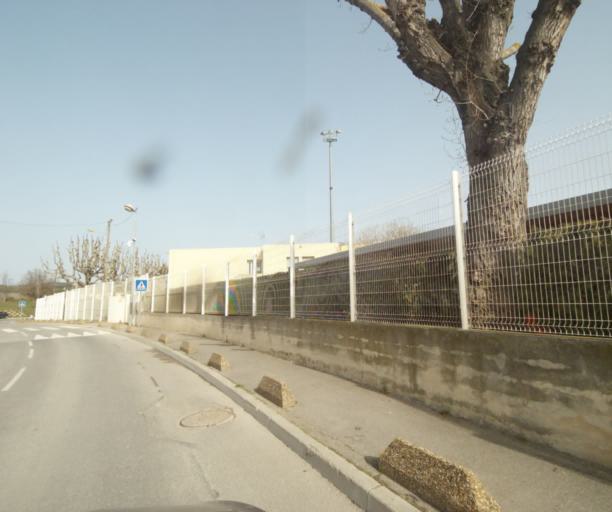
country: FR
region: Provence-Alpes-Cote d'Azur
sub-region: Departement des Bouches-du-Rhone
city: Meyreuil
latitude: 43.4710
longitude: 5.4974
